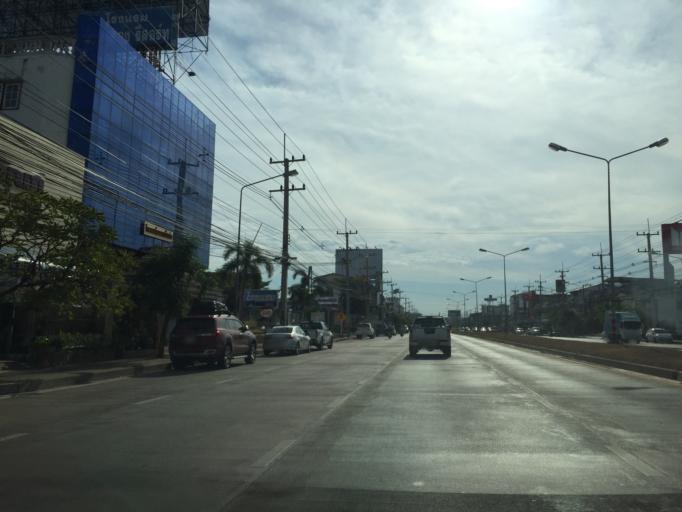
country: TH
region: Phitsanulok
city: Phitsanulok
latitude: 16.8363
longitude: 100.2413
